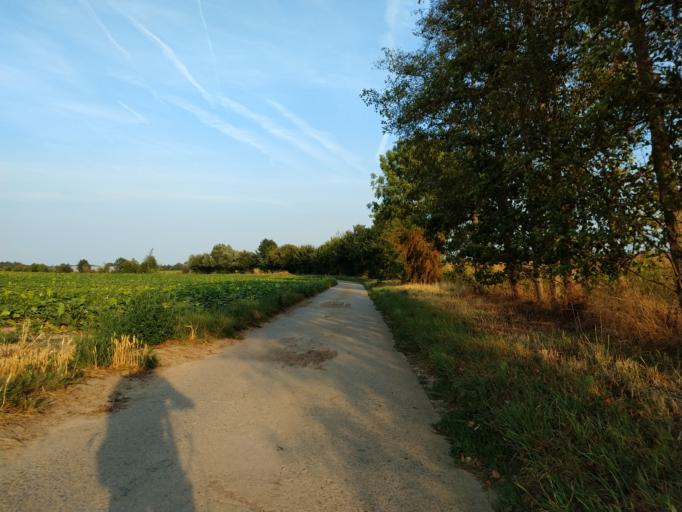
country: BE
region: Flanders
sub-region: Provincie Vlaams-Brabant
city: Hoegaarden
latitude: 50.7847
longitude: 4.8853
